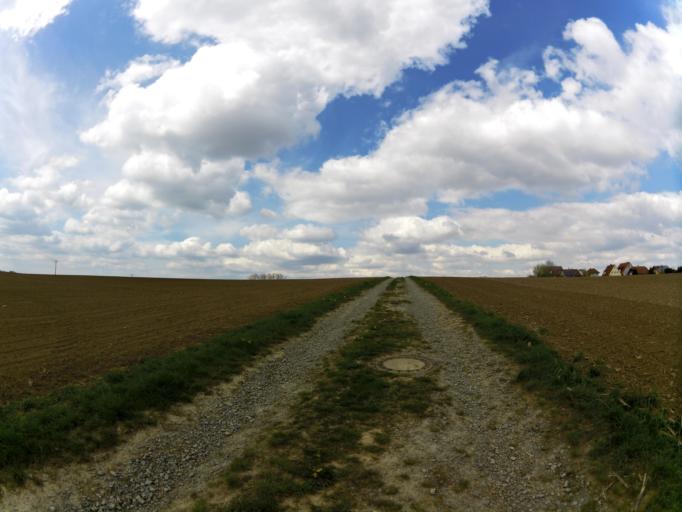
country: DE
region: Bavaria
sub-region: Regierungsbezirk Unterfranken
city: Giebelstadt
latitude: 49.6518
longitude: 9.9346
